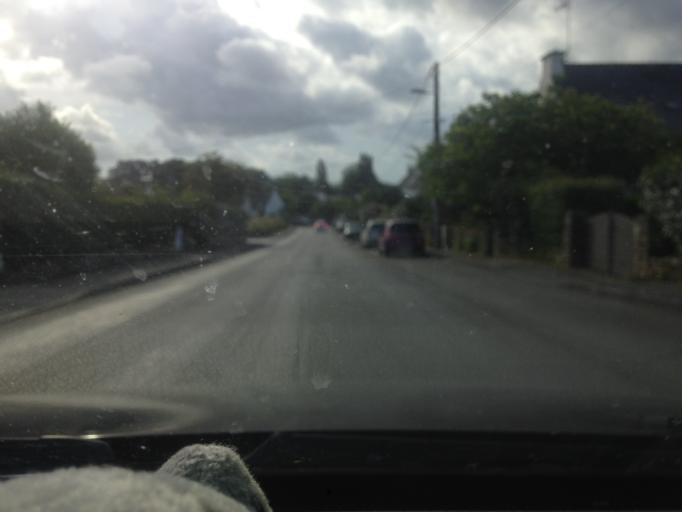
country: FR
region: Brittany
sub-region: Departement du Morbihan
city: Carnac
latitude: 47.5873
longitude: -3.0800
